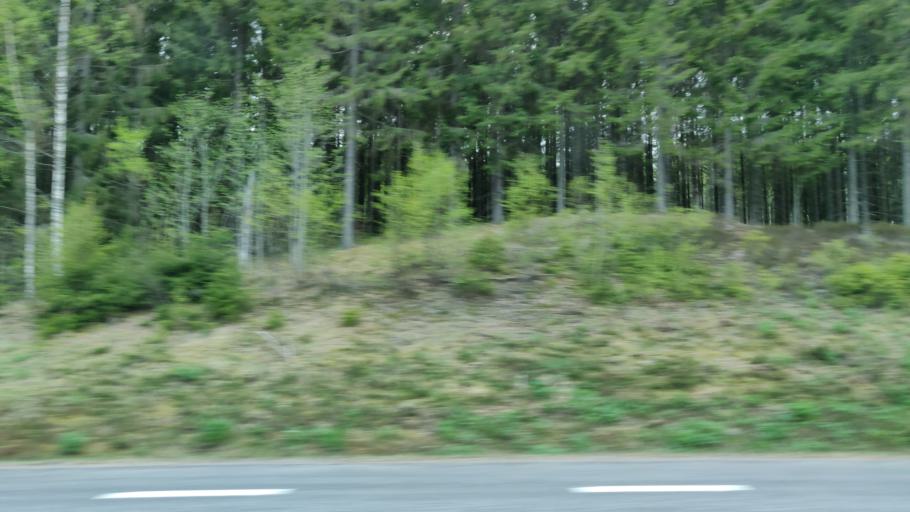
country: SE
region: Vaermland
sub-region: Munkfors Kommun
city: Munkfors
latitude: 59.7620
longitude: 13.4416
